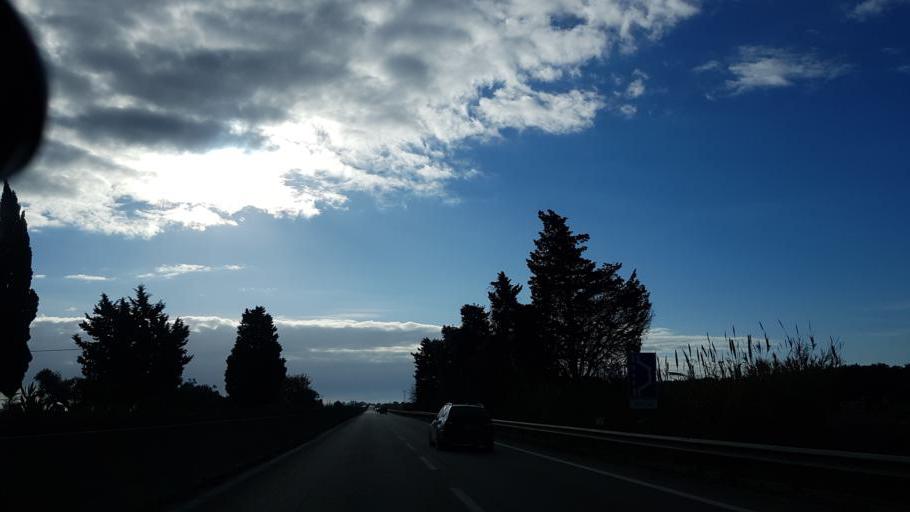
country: IT
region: Apulia
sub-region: Provincia di Brindisi
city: La Rosa
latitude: 40.5761
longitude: 17.9808
